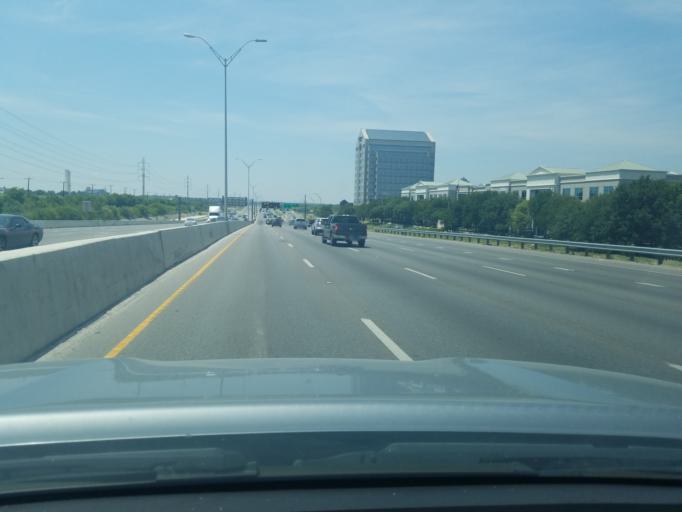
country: US
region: Texas
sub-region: Bexar County
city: Alamo Heights
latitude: 29.5074
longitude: -98.4781
